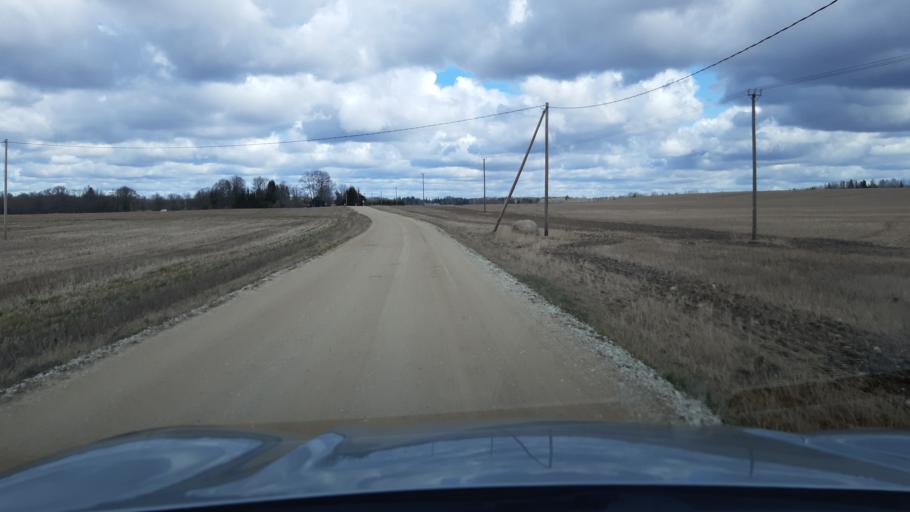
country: EE
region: Harju
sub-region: Rae vald
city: Vaida
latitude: 59.0823
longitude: 25.1292
